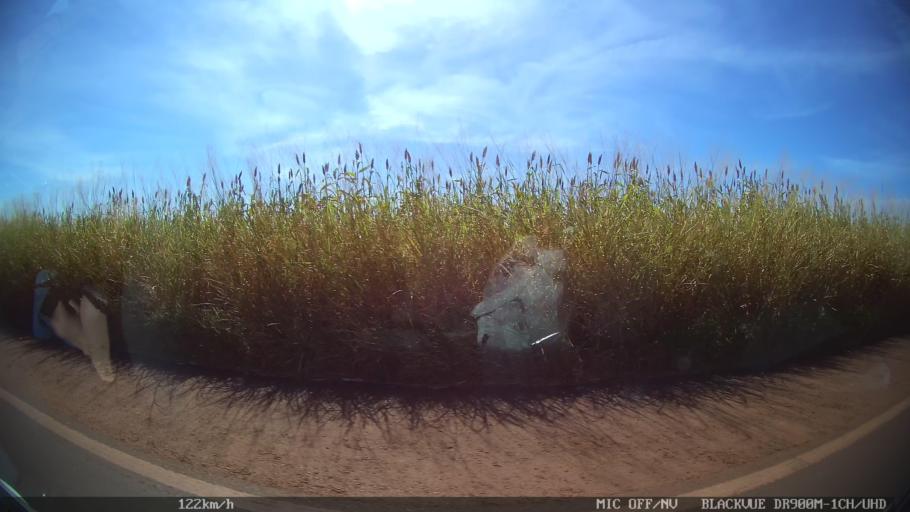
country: BR
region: Sao Paulo
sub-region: Sao Joaquim Da Barra
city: Sao Joaquim da Barra
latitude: -20.5580
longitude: -47.7044
